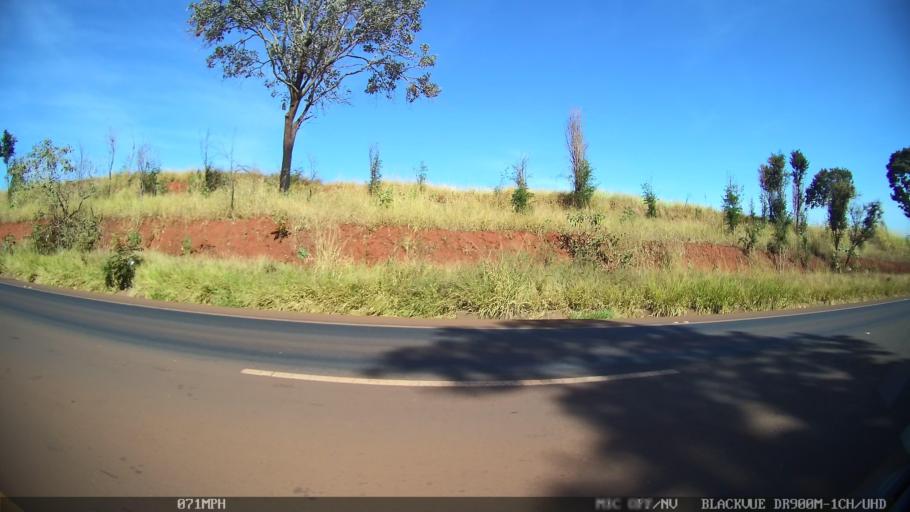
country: BR
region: Sao Paulo
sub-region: Sao Joaquim Da Barra
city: Sao Joaquim da Barra
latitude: -20.5499
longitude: -47.7497
